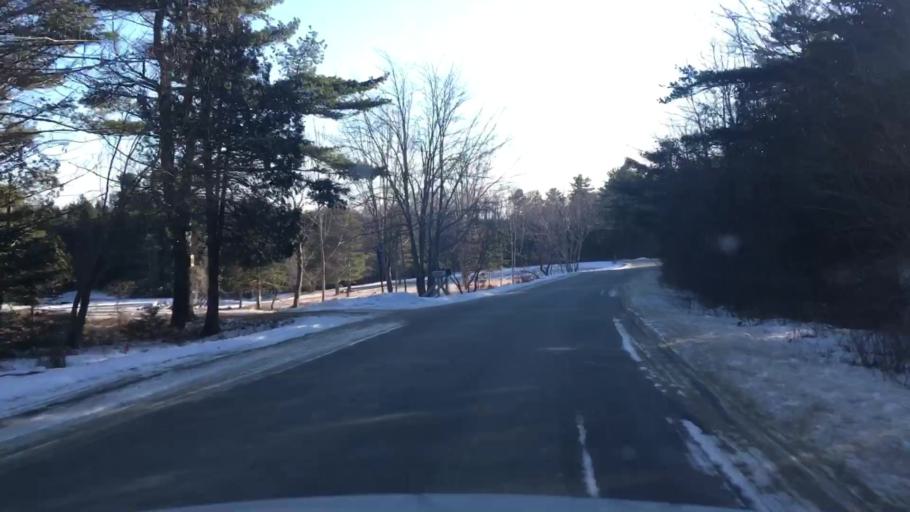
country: US
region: Maine
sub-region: Hancock County
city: Castine
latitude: 44.3430
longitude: -68.7830
